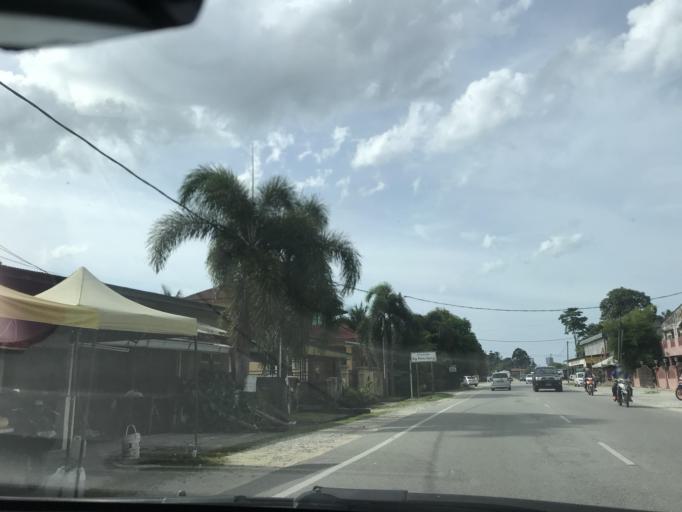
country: MY
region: Kelantan
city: Kota Bharu
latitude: 6.0872
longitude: 102.2278
